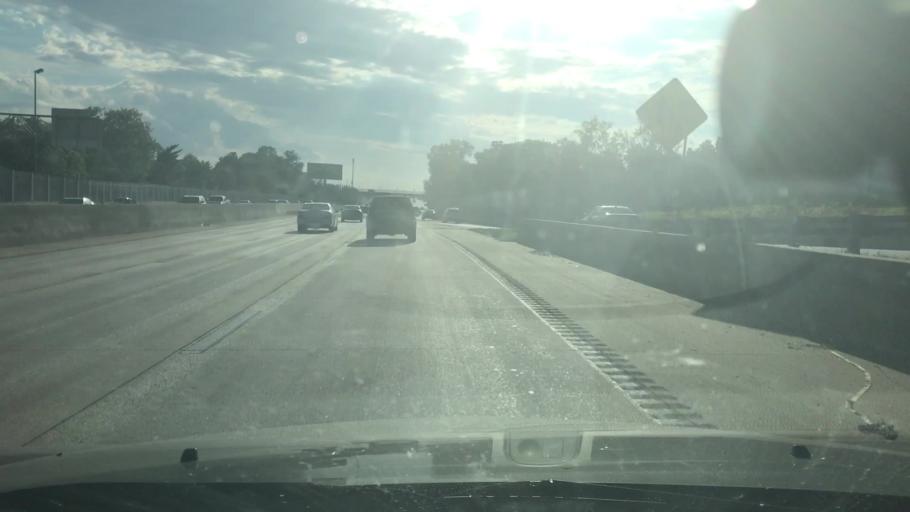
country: US
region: Missouri
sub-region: Saint Louis County
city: Richmond Heights
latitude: 38.6299
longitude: -90.3220
